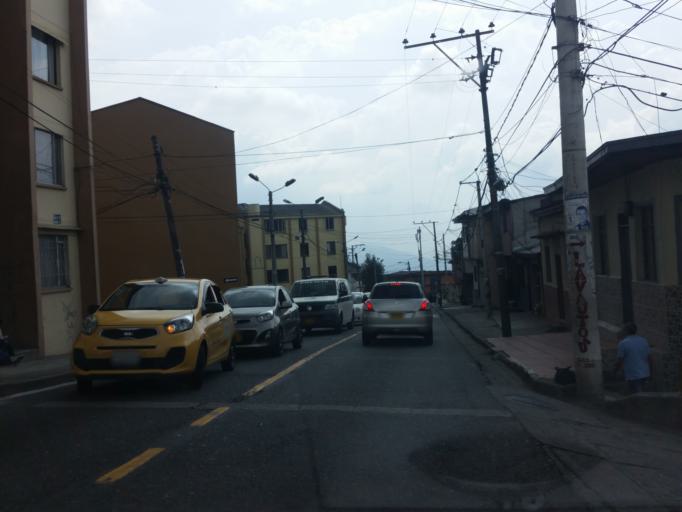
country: CO
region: Caldas
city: Manizales
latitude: 5.0641
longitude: -75.5080
